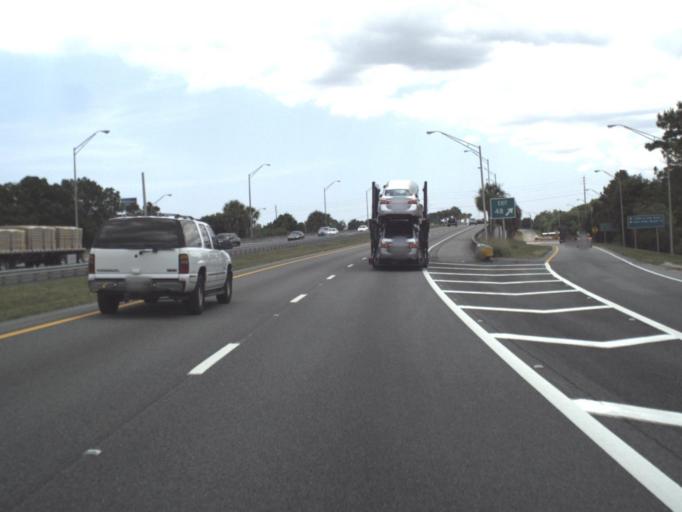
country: US
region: Florida
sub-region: Duval County
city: Jacksonville
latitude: 30.3274
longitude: -81.5290
